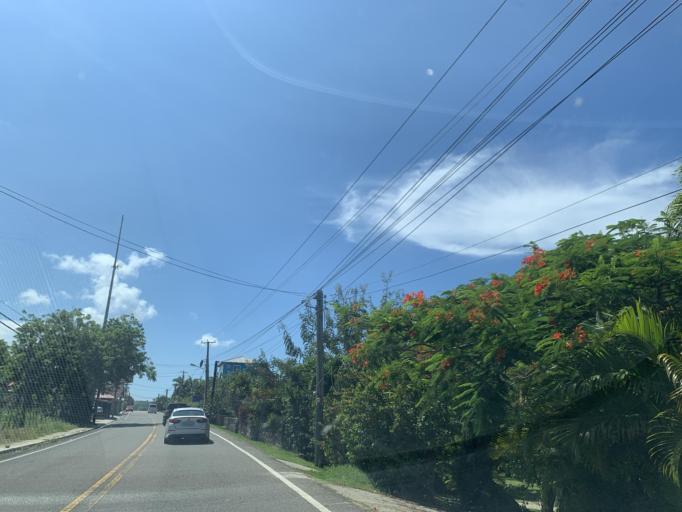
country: DO
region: Maria Trinidad Sanchez
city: Cabrera
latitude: 19.6710
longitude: -69.9562
